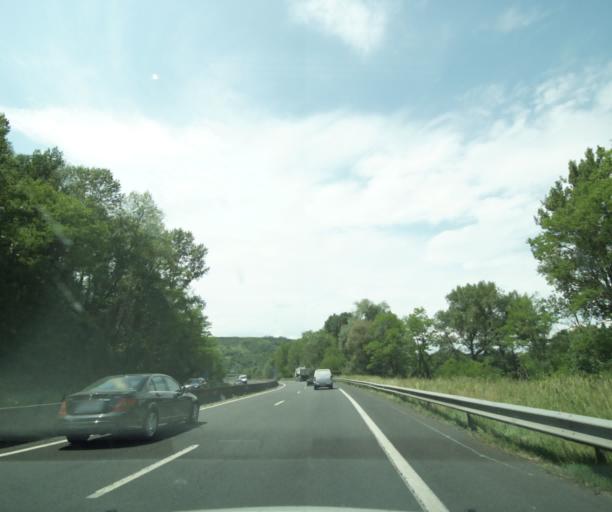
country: FR
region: Auvergne
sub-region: Departement du Puy-de-Dome
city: Issoire
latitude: 45.5948
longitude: 3.2261
